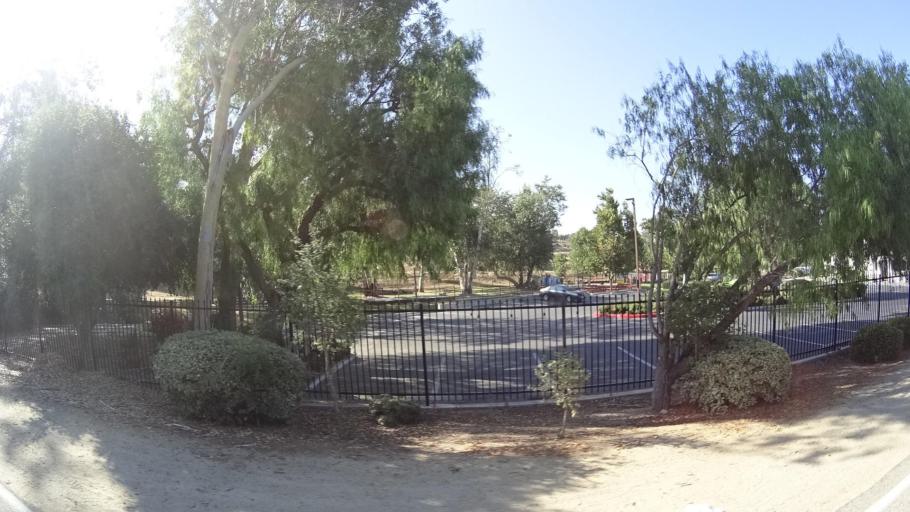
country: US
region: California
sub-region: San Diego County
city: Fallbrook
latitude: 33.3583
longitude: -117.2294
